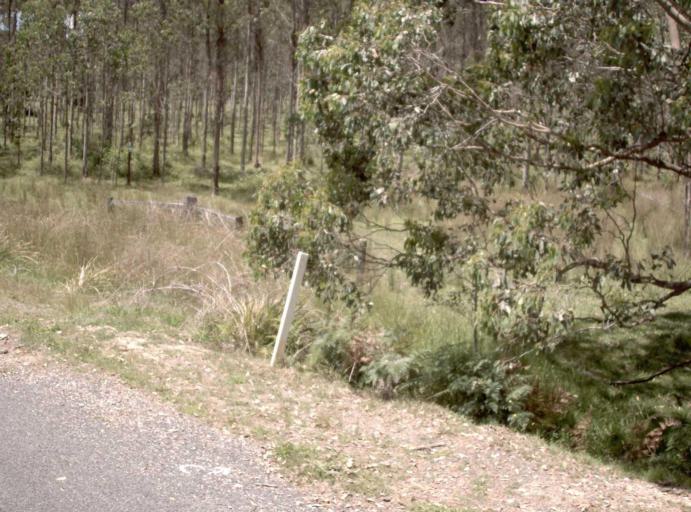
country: AU
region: New South Wales
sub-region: Bombala
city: Bombala
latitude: -37.3996
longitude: 149.0135
